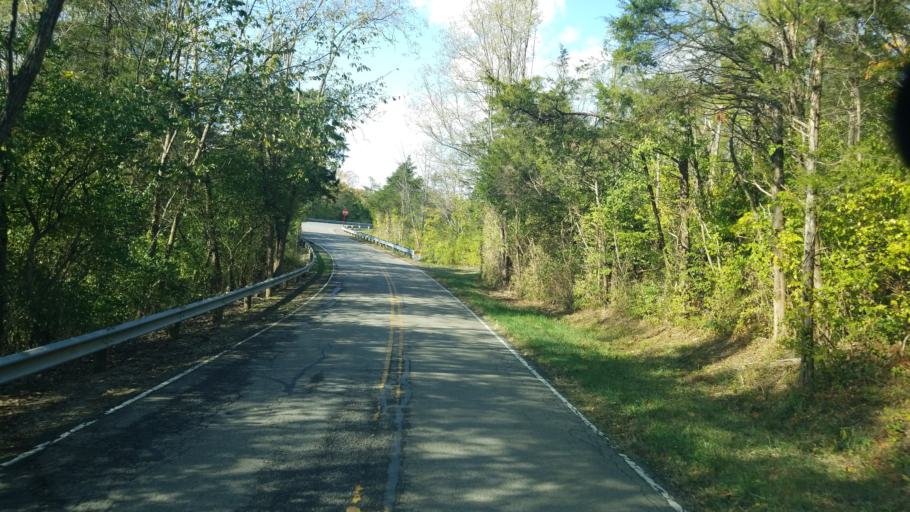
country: US
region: Ohio
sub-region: Warren County
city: Lebanon
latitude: 39.4019
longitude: -84.1748
